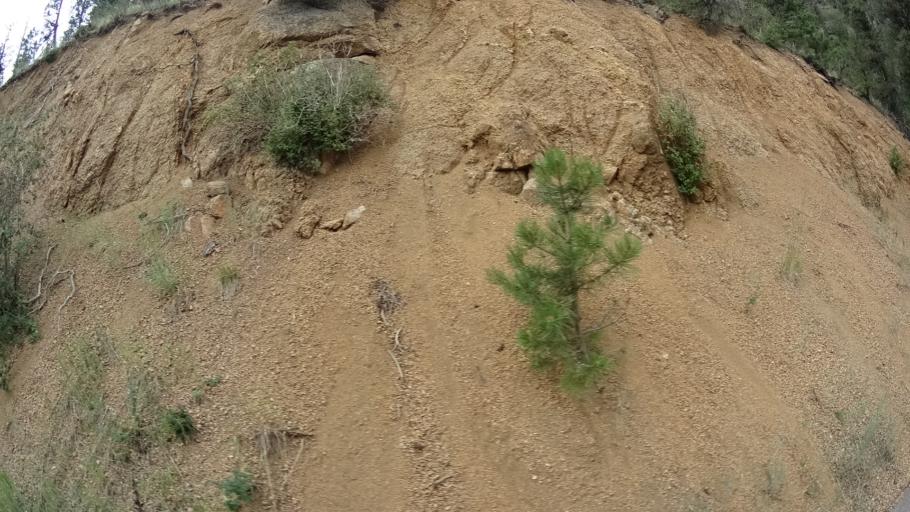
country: US
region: Colorado
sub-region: El Paso County
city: Cascade-Chipita Park
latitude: 38.9011
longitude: -104.9806
